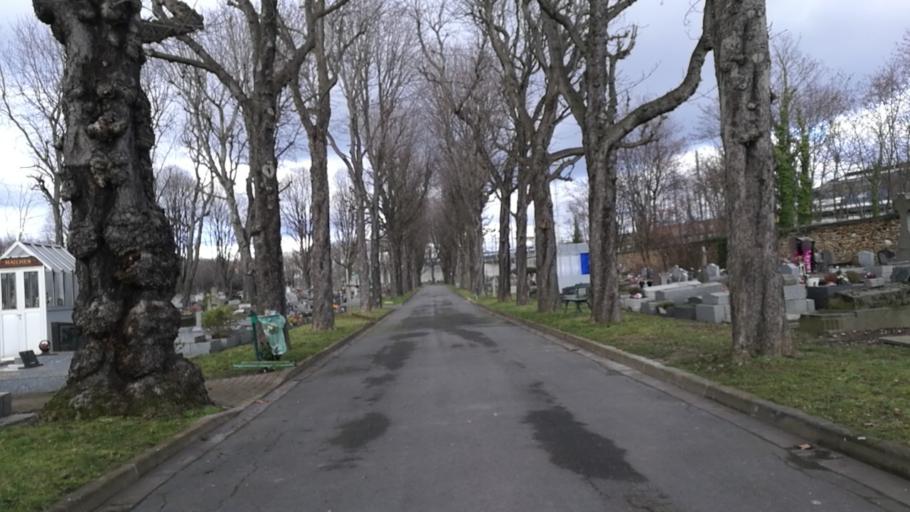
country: FR
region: Ile-de-France
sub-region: Paris
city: Saint-Ouen
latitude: 48.9065
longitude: 2.3503
